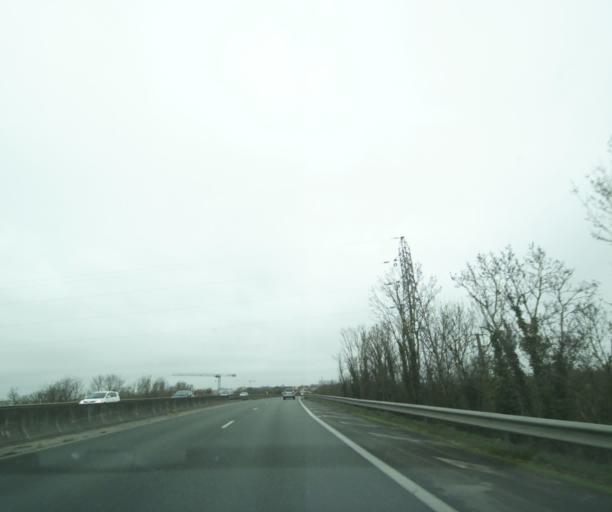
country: FR
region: Poitou-Charentes
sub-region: Departement de la Charente-Maritime
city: Perigny
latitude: 46.1610
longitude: -1.1215
